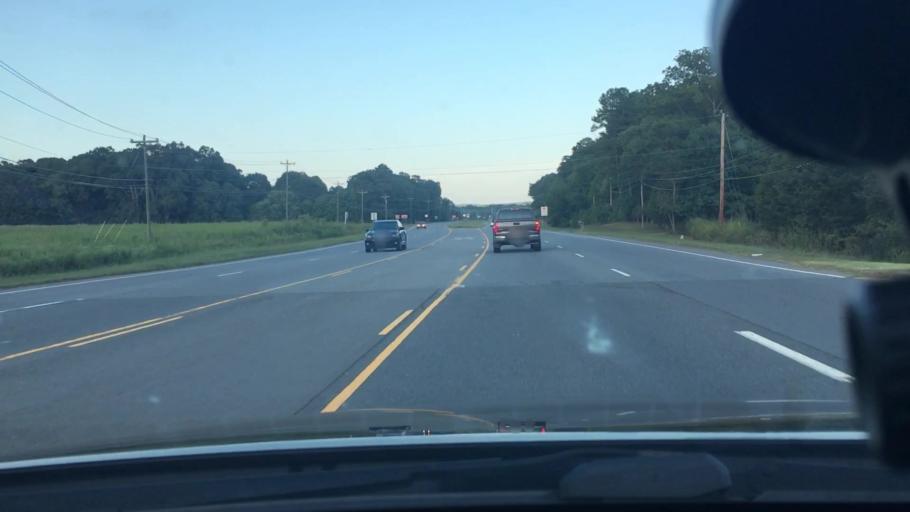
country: US
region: North Carolina
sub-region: Cabarrus County
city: Midland
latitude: 35.2539
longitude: -80.4877
